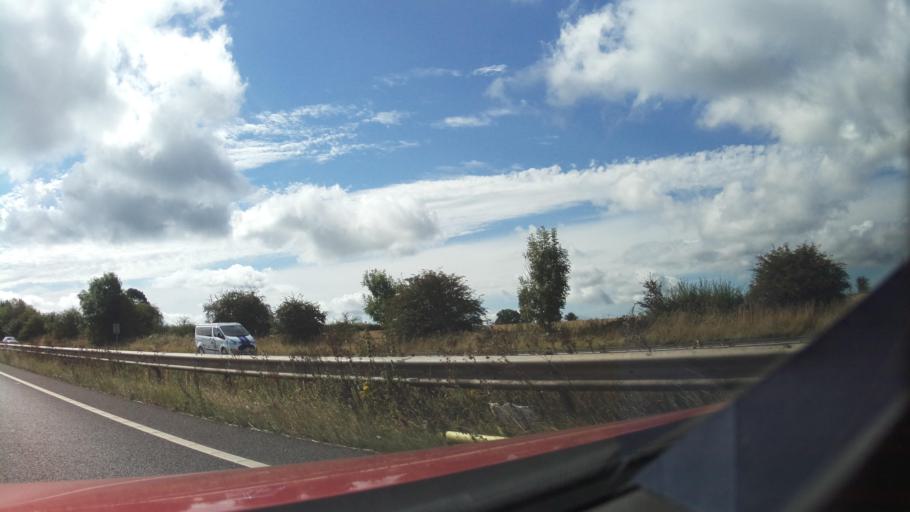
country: GB
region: England
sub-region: Derbyshire
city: Alfreton
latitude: 53.0829
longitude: -1.4089
